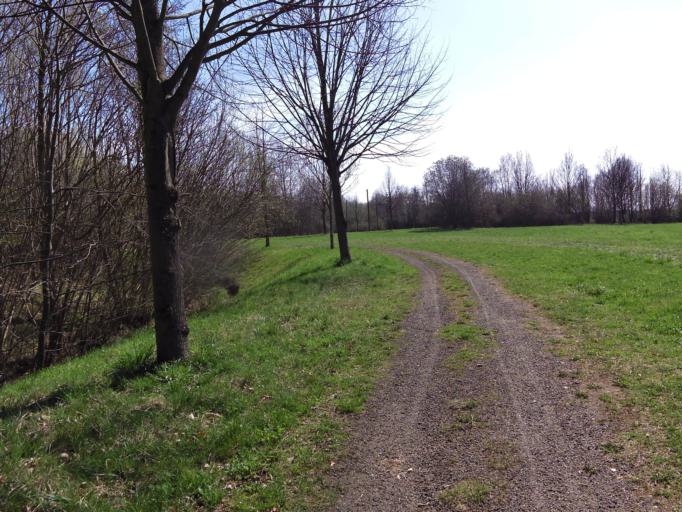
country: DE
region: Saxony
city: Schkeuditz
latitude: 51.3872
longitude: 12.2895
